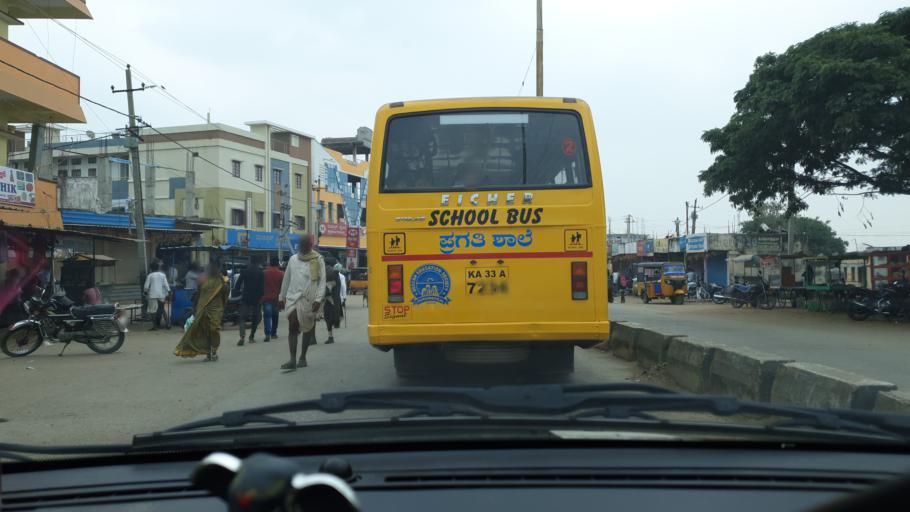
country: IN
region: Karnataka
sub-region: Yadgir
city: Gurmatkal
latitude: 16.8719
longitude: 77.3909
